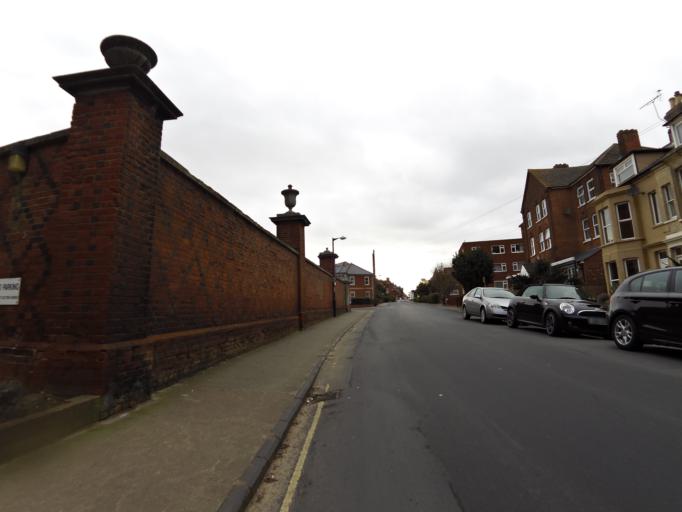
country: GB
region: England
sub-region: Suffolk
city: Felixstowe
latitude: 51.9625
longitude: 1.3575
